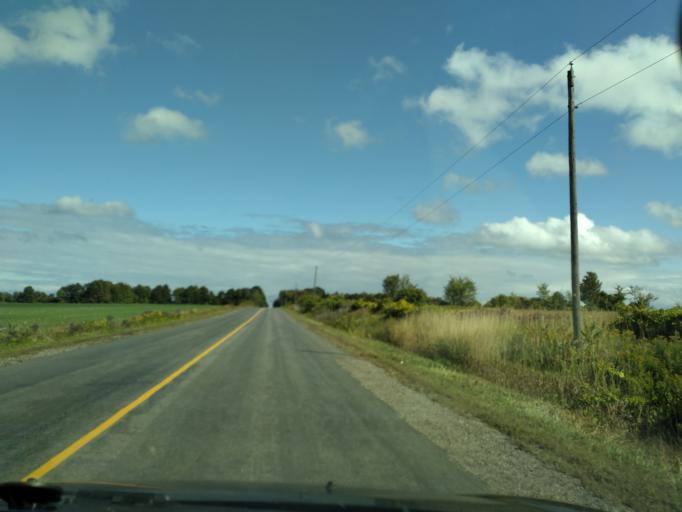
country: CA
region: Ontario
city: Innisfil
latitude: 44.2825
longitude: -79.5800
